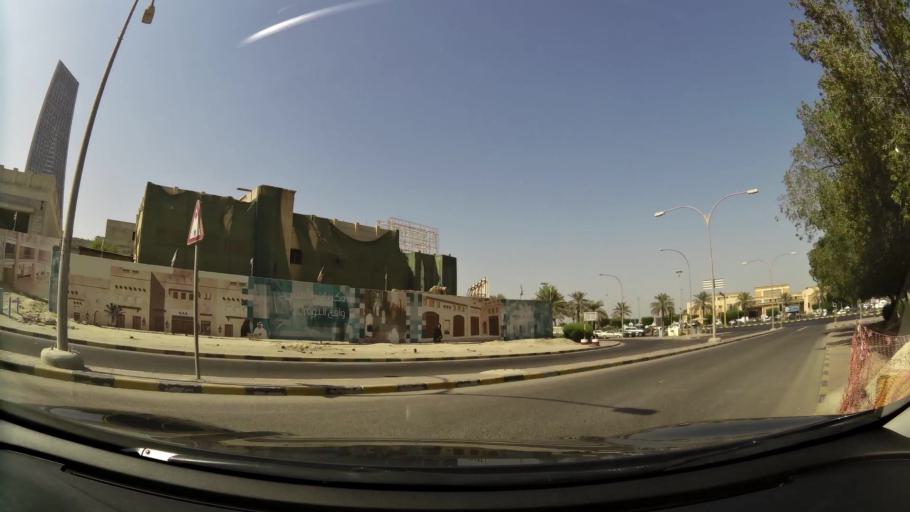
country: KW
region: Al Asimah
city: Kuwait City
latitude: 29.3848
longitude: 47.9805
